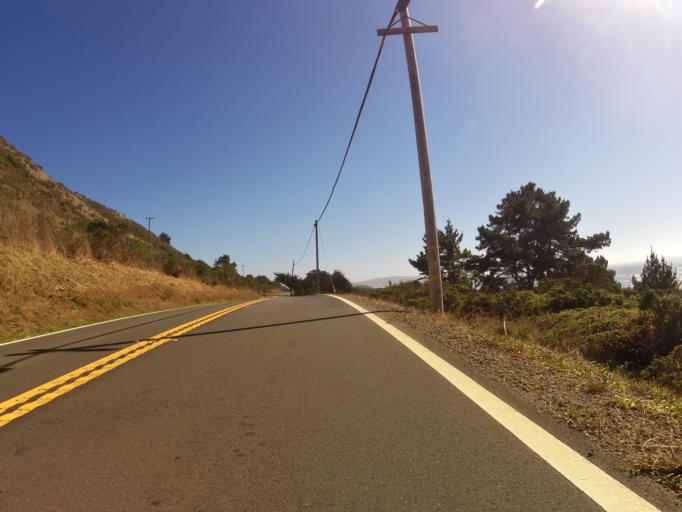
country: US
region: California
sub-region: Mendocino County
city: Fort Bragg
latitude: 39.5973
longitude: -123.7834
